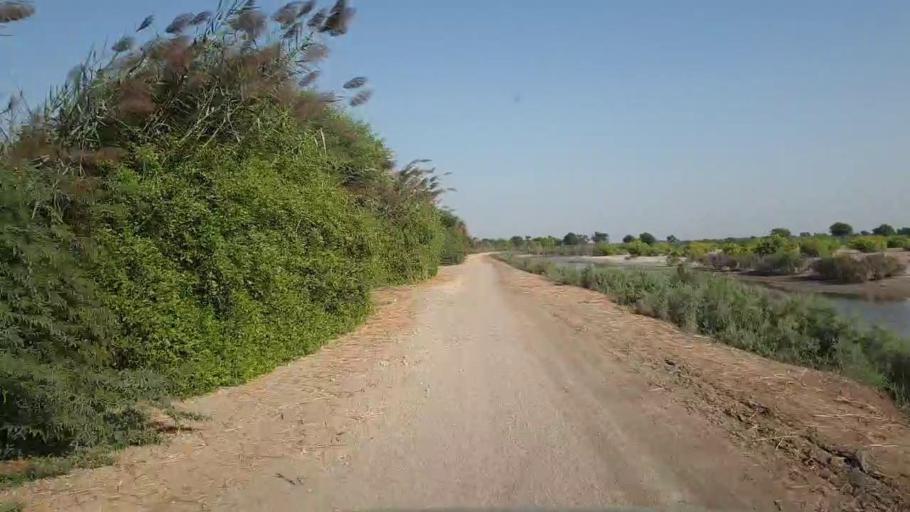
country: PK
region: Sindh
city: Matli
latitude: 25.0040
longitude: 68.7448
